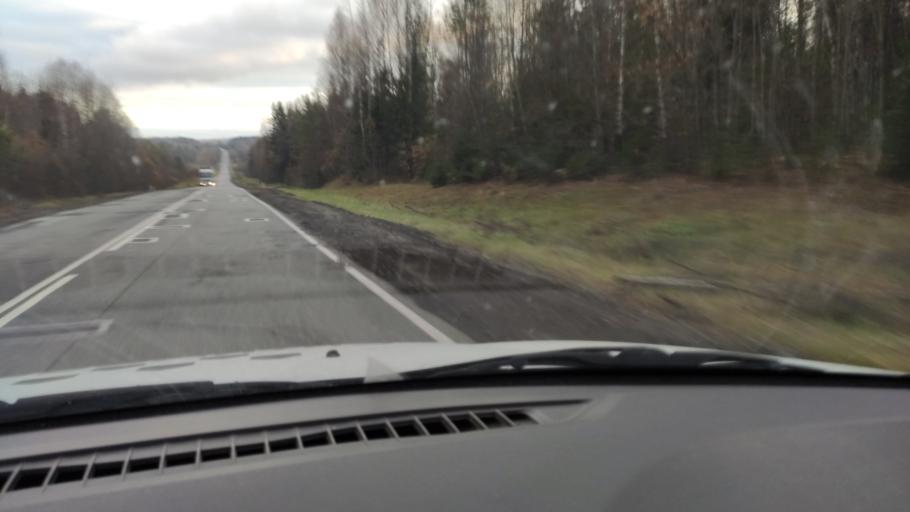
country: RU
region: Kirov
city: Omutninsk
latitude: 58.7351
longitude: 52.0727
